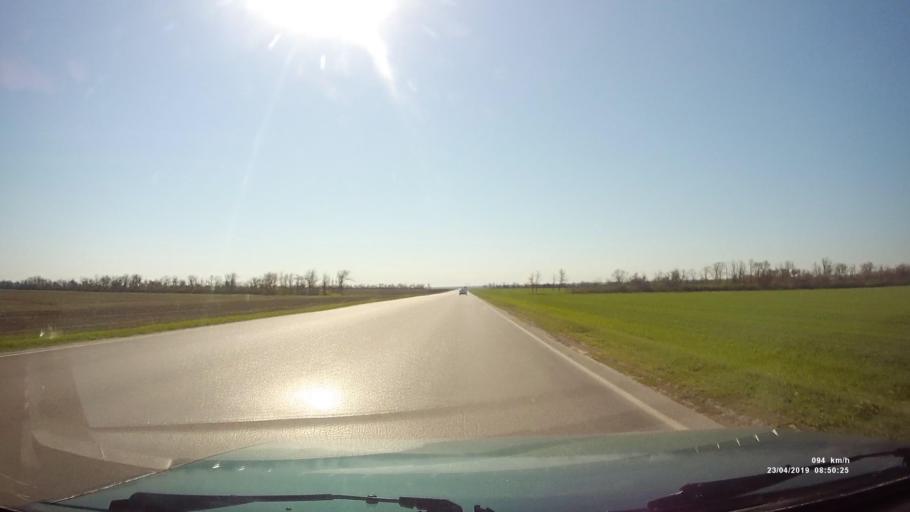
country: RU
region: Rostov
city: Gigant
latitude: 46.4970
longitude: 41.4271
